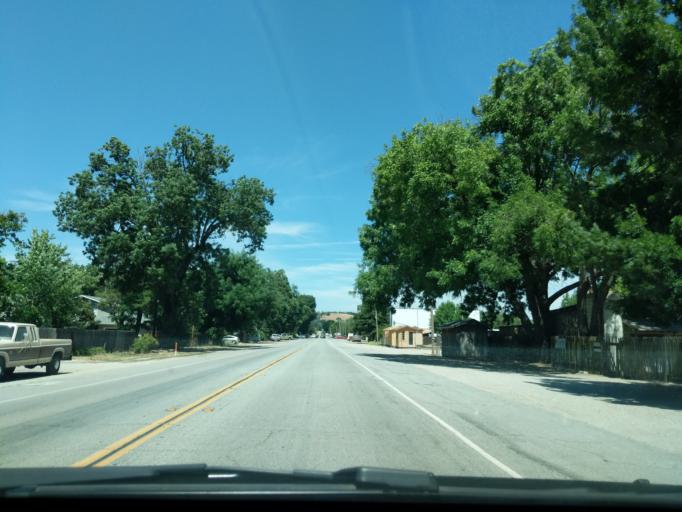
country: US
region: California
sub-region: San Luis Obispo County
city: Santa Margarita
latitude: 35.3872
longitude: -120.6159
